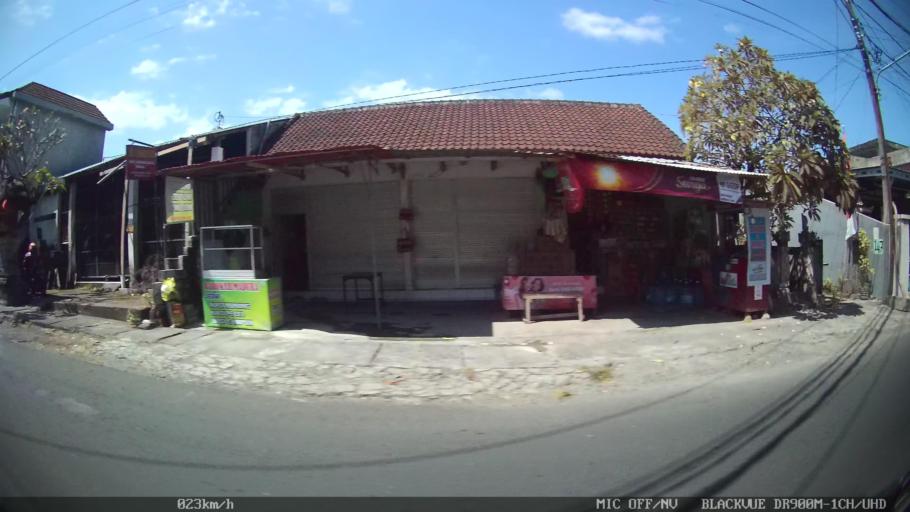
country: ID
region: Bali
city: Denpasar
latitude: -8.6706
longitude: 115.1833
